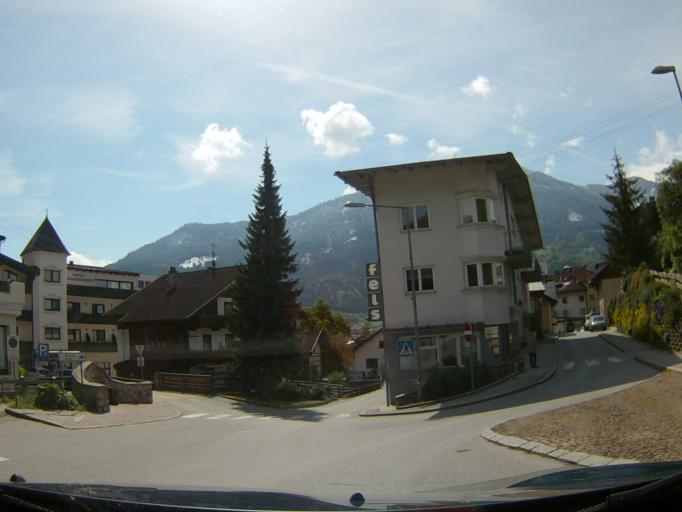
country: AT
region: Tyrol
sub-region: Politischer Bezirk Schwaz
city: Jenbach
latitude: 47.3929
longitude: 11.7719
